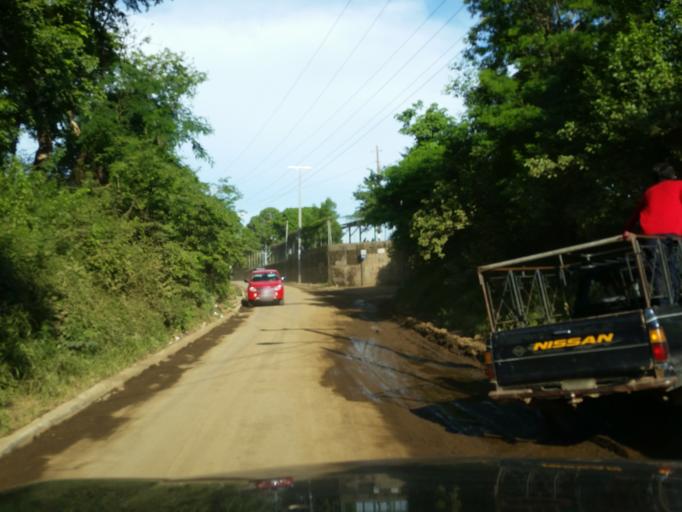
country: NI
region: Managua
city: Managua
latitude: 12.0970
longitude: -86.2079
